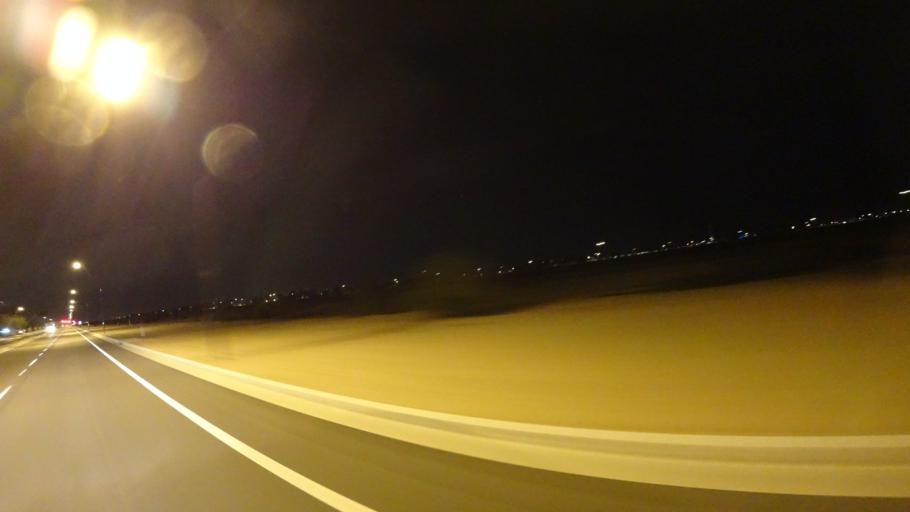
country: US
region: Arizona
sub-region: Maricopa County
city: Queen Creek
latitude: 33.2634
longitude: -111.6464
